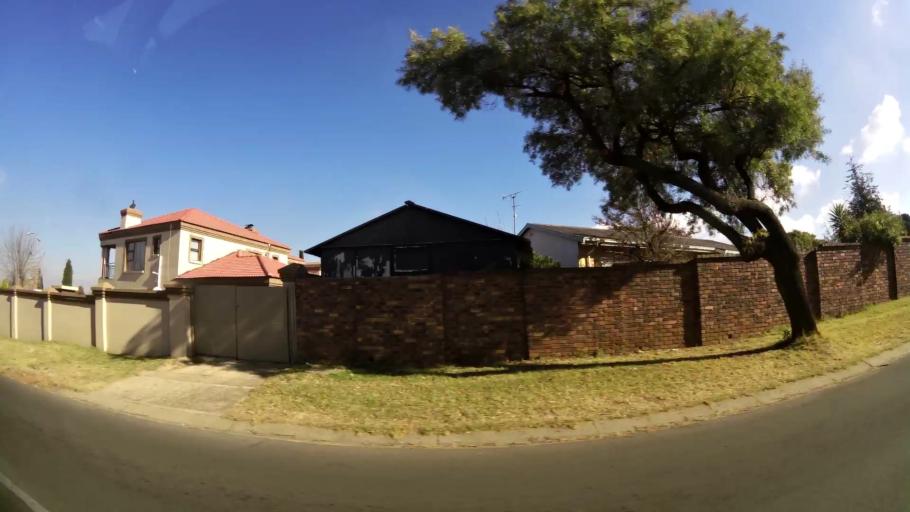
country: ZA
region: Gauteng
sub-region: City of Johannesburg Metropolitan Municipality
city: Roodepoort
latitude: -26.1602
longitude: 27.8260
